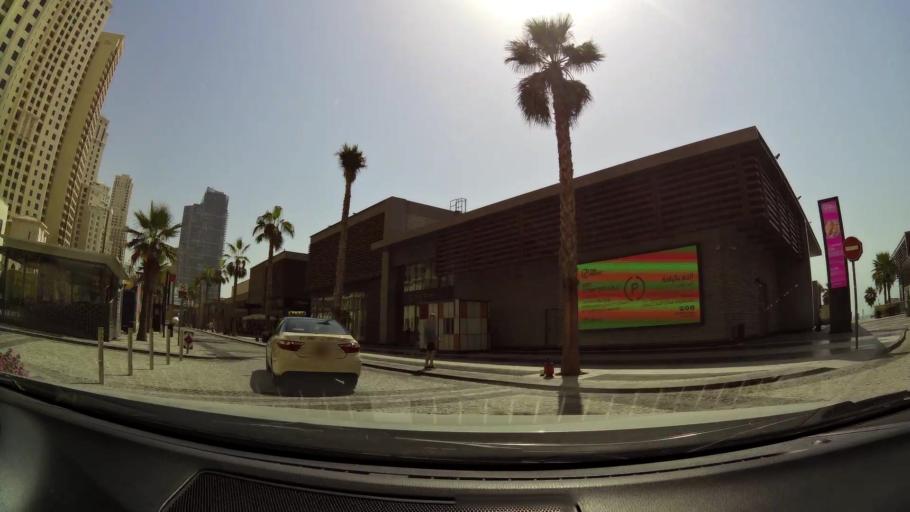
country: AE
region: Dubai
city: Dubai
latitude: 25.0771
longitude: 55.1331
